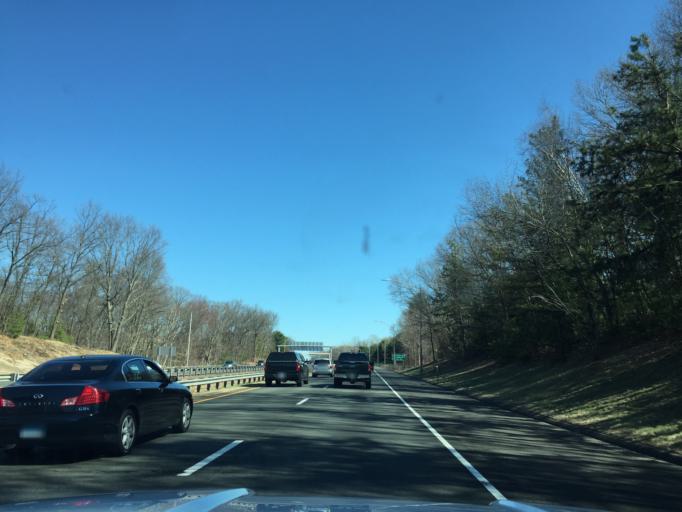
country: US
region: Connecticut
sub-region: Hartford County
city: Windsor Locks
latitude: 41.9111
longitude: -72.6676
